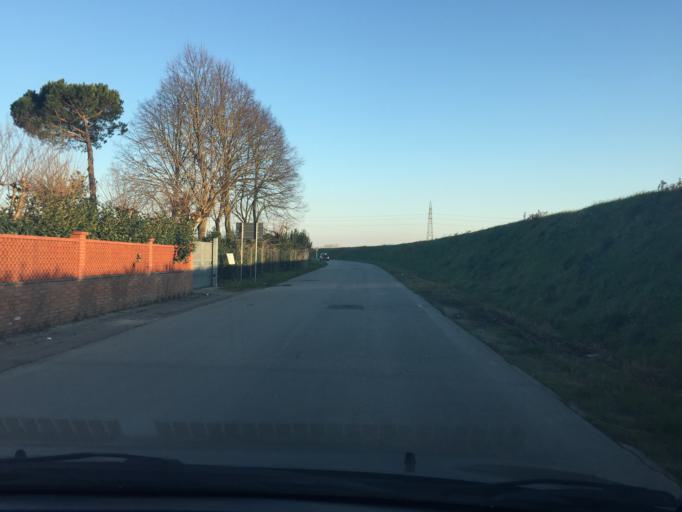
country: IT
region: Tuscany
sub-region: Provincia di Pistoia
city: Ponte Buggianese
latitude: 43.8383
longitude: 10.7525
